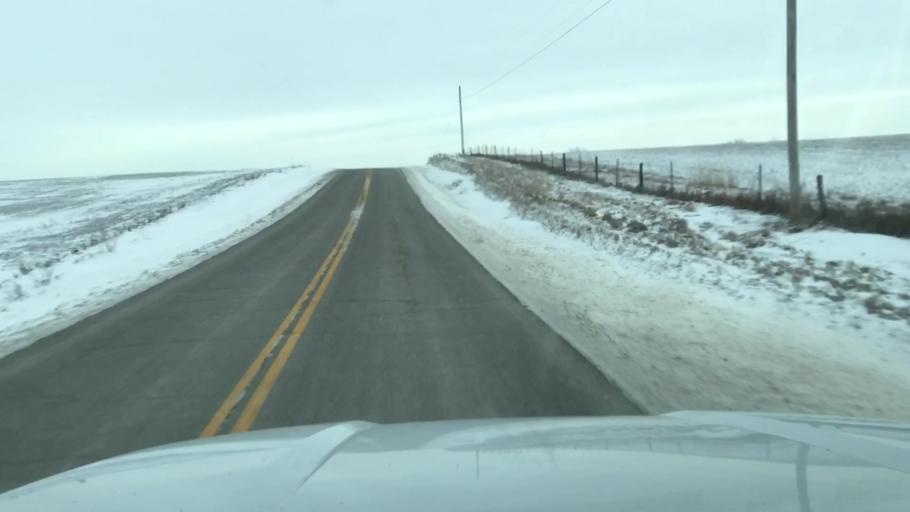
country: US
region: Missouri
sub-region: Holt County
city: Oregon
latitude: 40.0892
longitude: -94.9744
